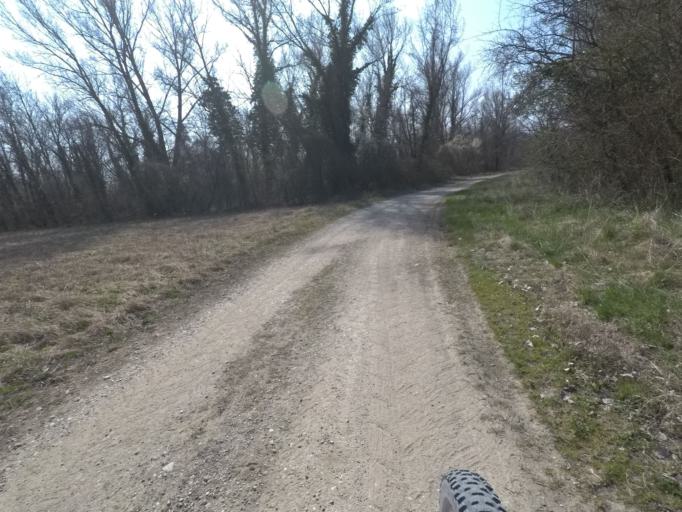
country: IT
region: Friuli Venezia Giulia
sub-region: Provincia di Udine
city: Remanzacco
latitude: 46.0641
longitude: 13.3288
